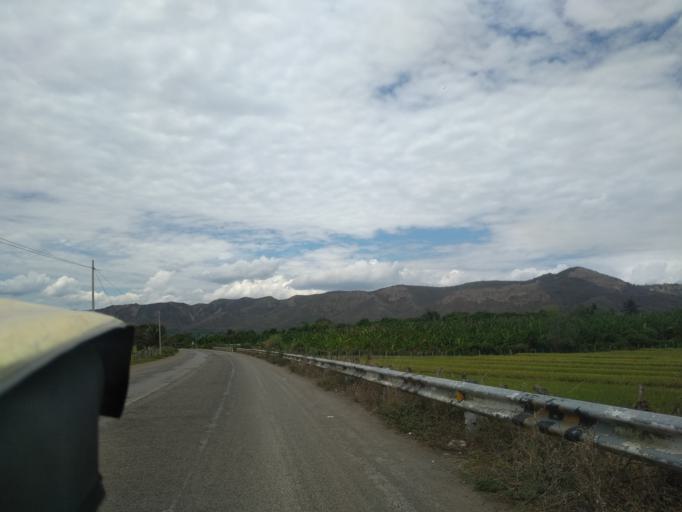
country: PE
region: Cajamarca
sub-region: Provincia de San Ignacio
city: La Coipa
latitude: -5.3475
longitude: -78.7963
